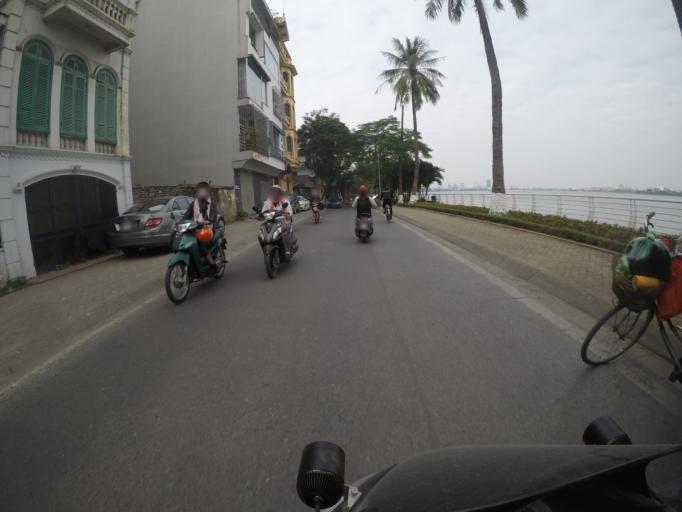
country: VN
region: Ha Noi
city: Tay Ho
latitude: 21.0515
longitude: 105.8129
